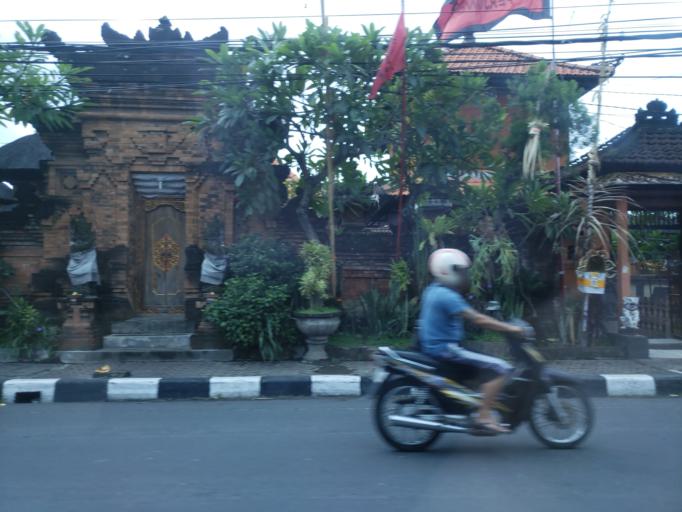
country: ID
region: Bali
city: Dajan Tangluk
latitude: -8.6467
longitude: 115.2438
